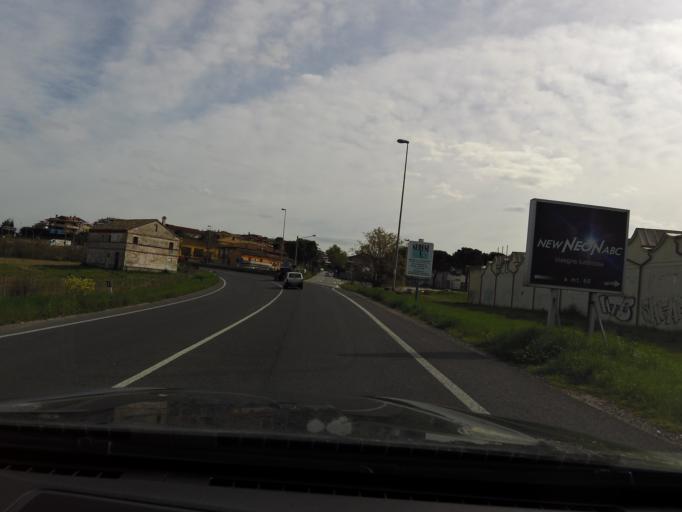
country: IT
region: The Marches
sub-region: Provincia di Ancona
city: Camerano
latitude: 43.4984
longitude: 13.5363
